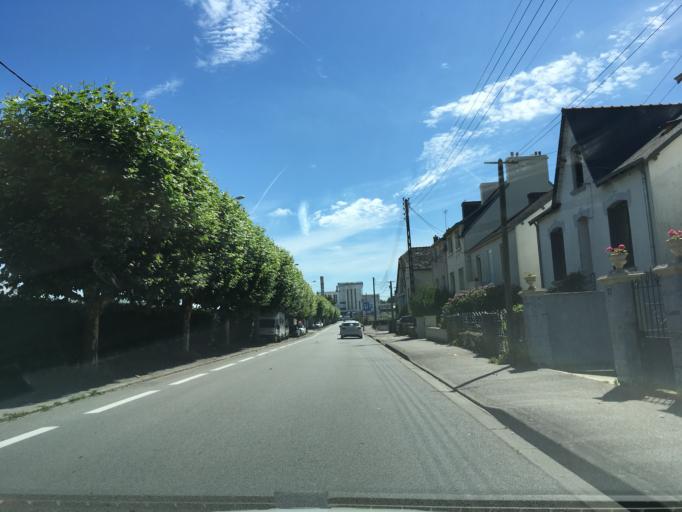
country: FR
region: Brittany
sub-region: Departement du Finistere
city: Quimper
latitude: 47.9959
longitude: -4.0804
